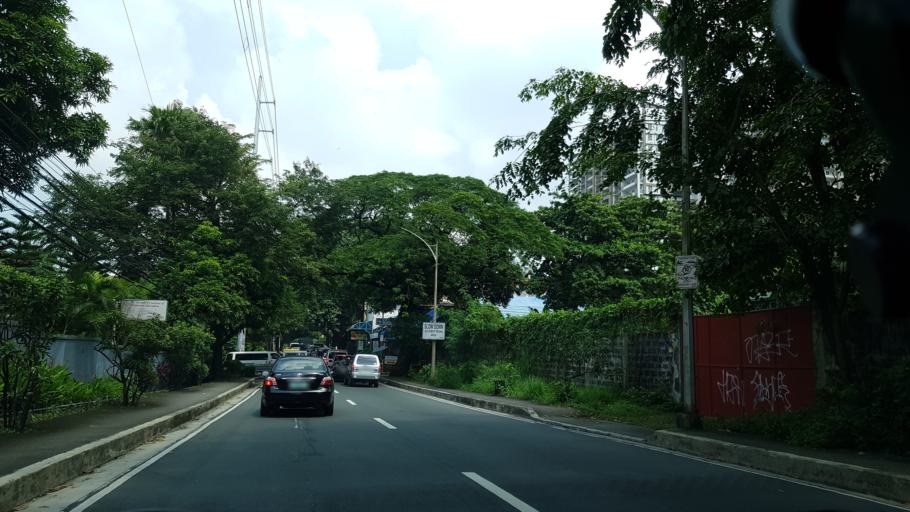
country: PH
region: Metro Manila
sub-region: San Juan
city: San Juan
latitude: 14.6217
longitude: 121.0328
